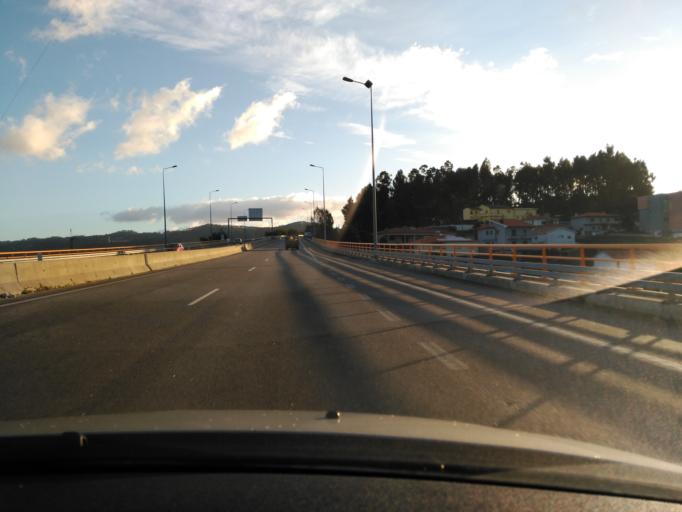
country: PT
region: Braga
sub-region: Guimaraes
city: Guimaraes
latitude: 41.4556
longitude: -8.2714
